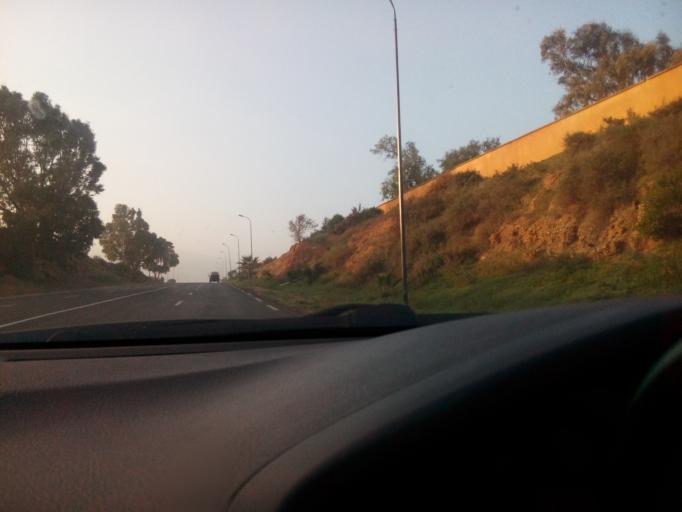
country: DZ
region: Oran
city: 'Ain el Turk
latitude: 35.7168
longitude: -0.8532
